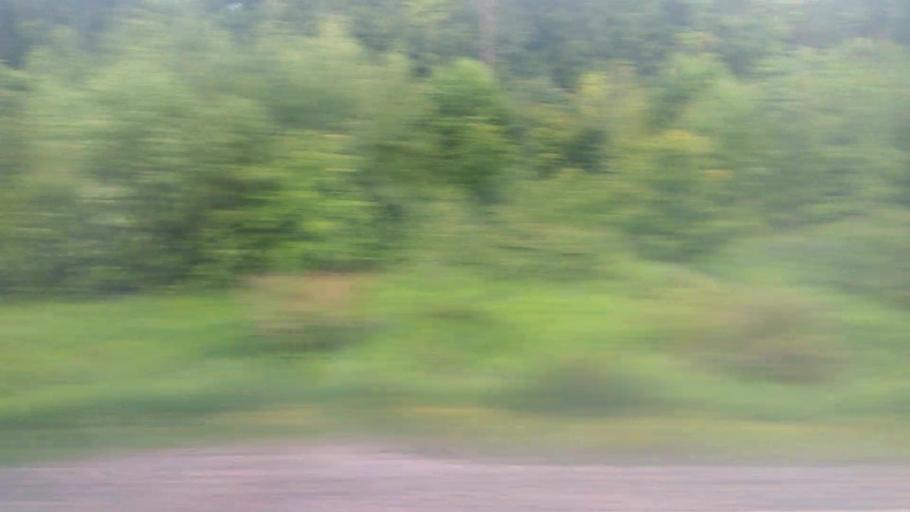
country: RU
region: Moskovskaya
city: Mikhnevo
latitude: 55.0919
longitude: 37.9680
